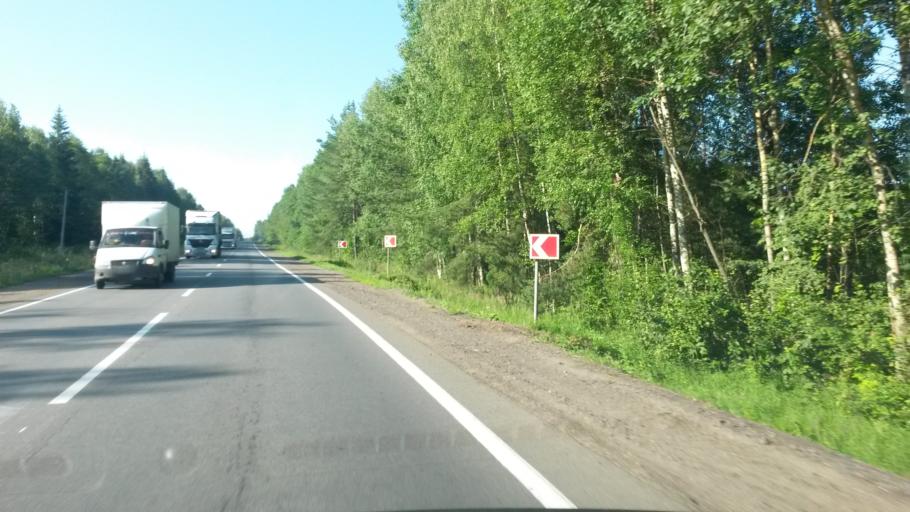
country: RU
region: Jaroslavl
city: Gavrilov-Yam
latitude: 57.2779
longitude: 39.9512
